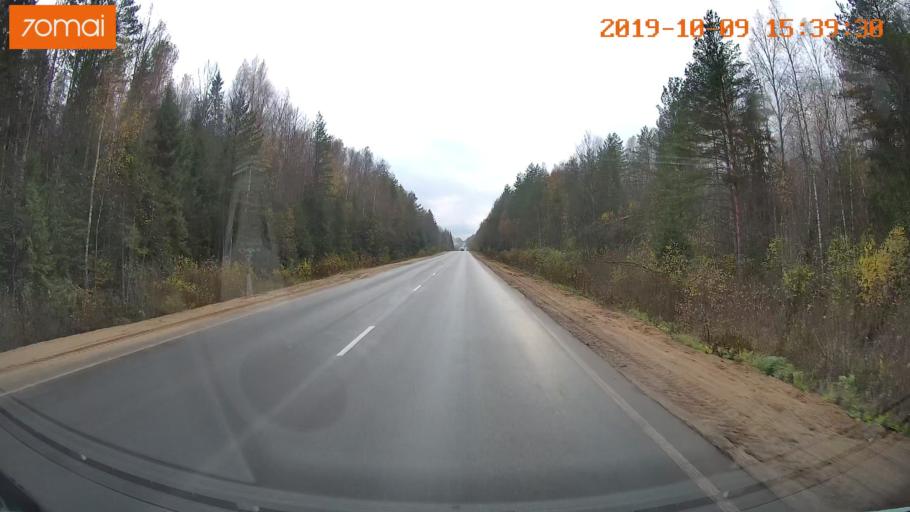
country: RU
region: Kostroma
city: Oktyabr'skiy
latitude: 57.8965
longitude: 41.1634
